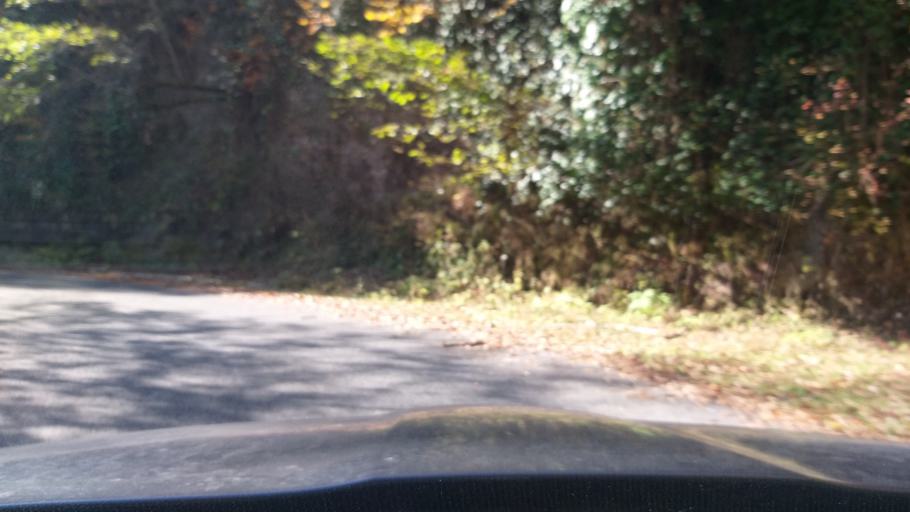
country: GE
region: Abkhazia
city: Bich'vinta
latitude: 43.1935
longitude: 40.4558
